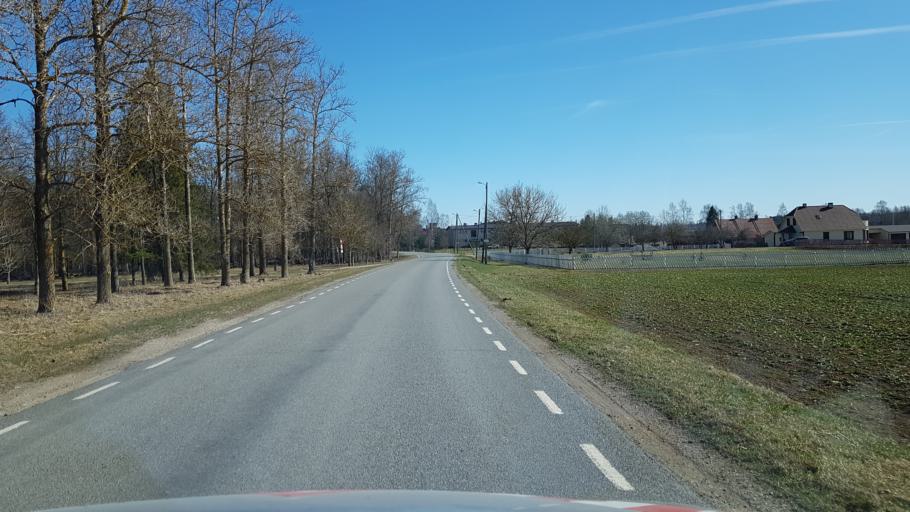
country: EE
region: Laeaene-Virumaa
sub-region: Someru vald
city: Someru
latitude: 59.3437
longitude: 26.5072
